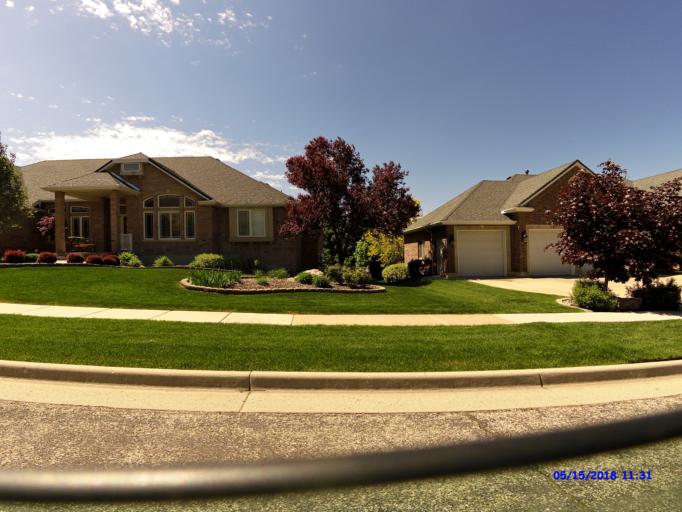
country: US
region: Utah
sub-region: Weber County
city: Uintah
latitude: 41.1739
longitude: -111.9369
